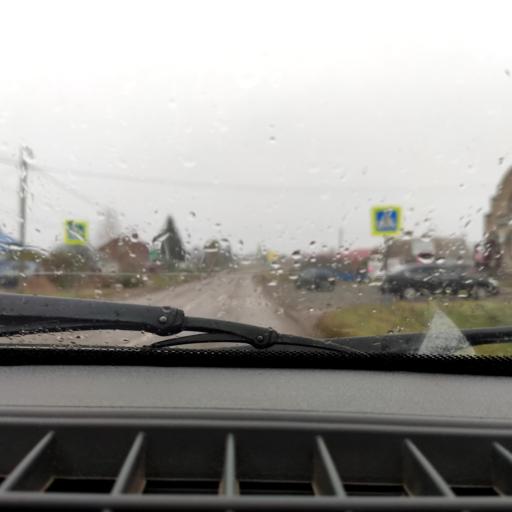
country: RU
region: Bashkortostan
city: Avdon
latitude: 54.6543
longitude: 55.7729
